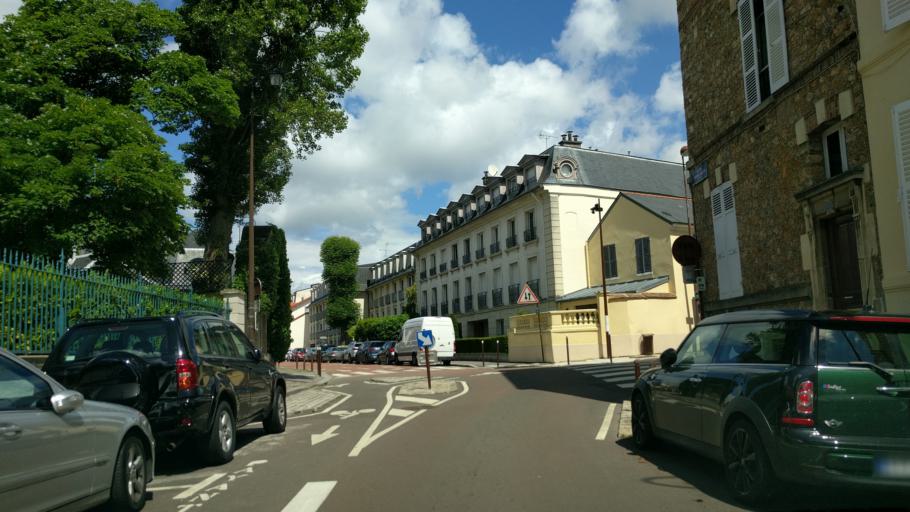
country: FR
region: Ile-de-France
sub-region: Departement des Yvelines
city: Le Chesnay
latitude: 48.8126
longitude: 2.1241
